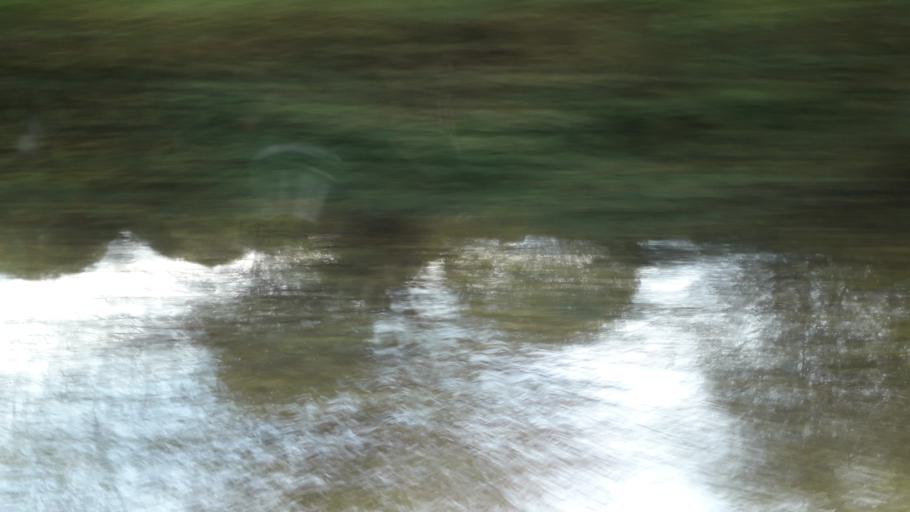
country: IE
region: Leinster
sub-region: An Longfort
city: Lanesborough
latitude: 53.7475
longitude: -7.9426
